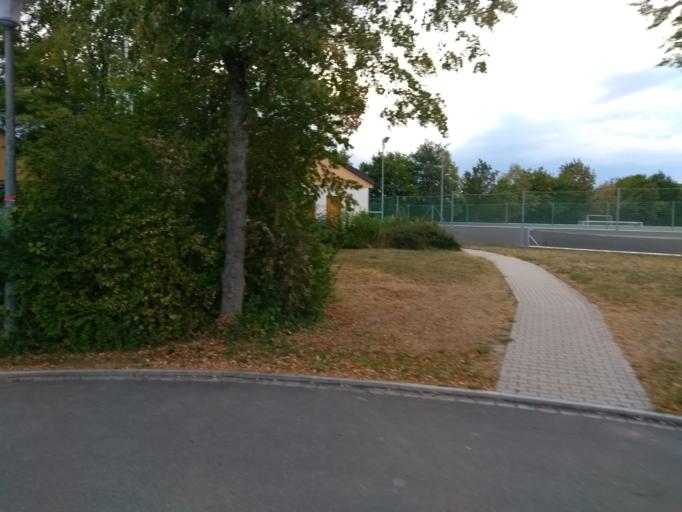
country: DE
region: Bavaria
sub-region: Regierungsbezirk Mittelfranken
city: Hagenbuchach
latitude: 49.5380
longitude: 10.7724
